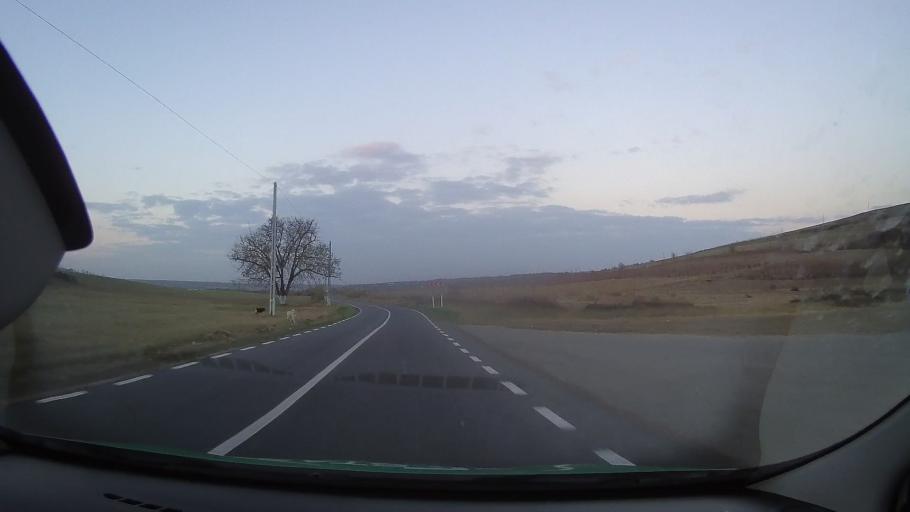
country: RO
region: Constanta
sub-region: Comuna Oltina
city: Oltina
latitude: 44.1508
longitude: 27.6676
